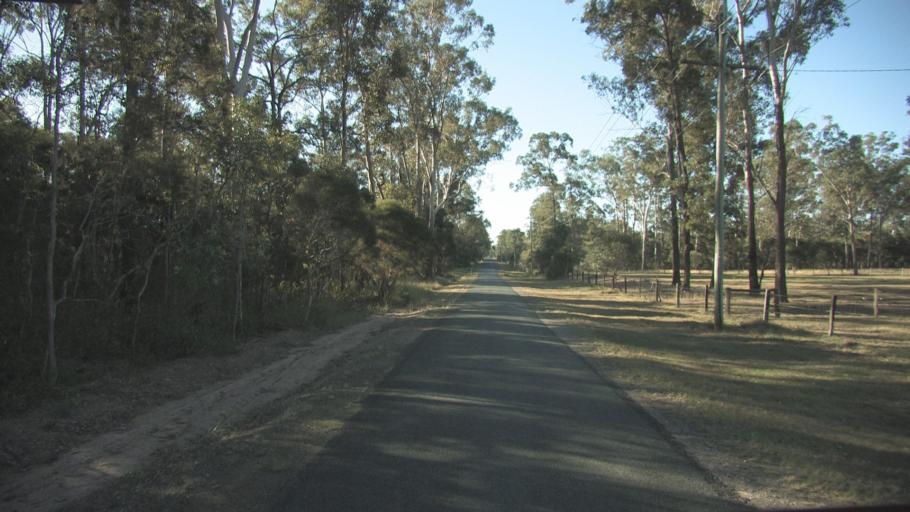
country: AU
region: Queensland
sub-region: Logan
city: North Maclean
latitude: -27.7848
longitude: 153.0457
